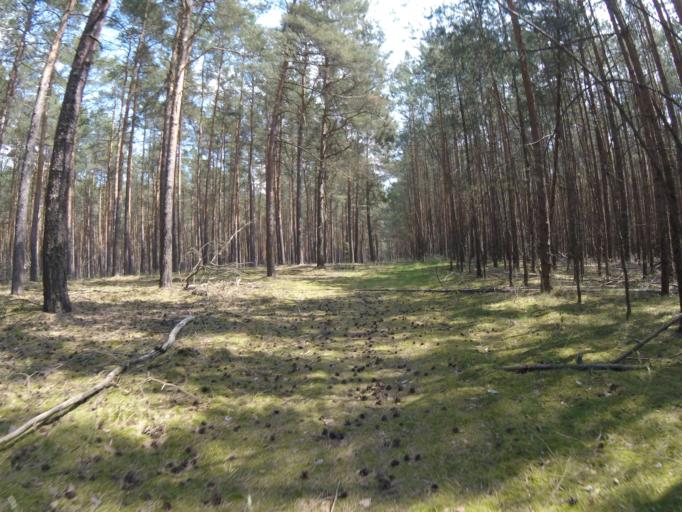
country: DE
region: Brandenburg
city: Bestensee
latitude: 52.2134
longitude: 13.6562
